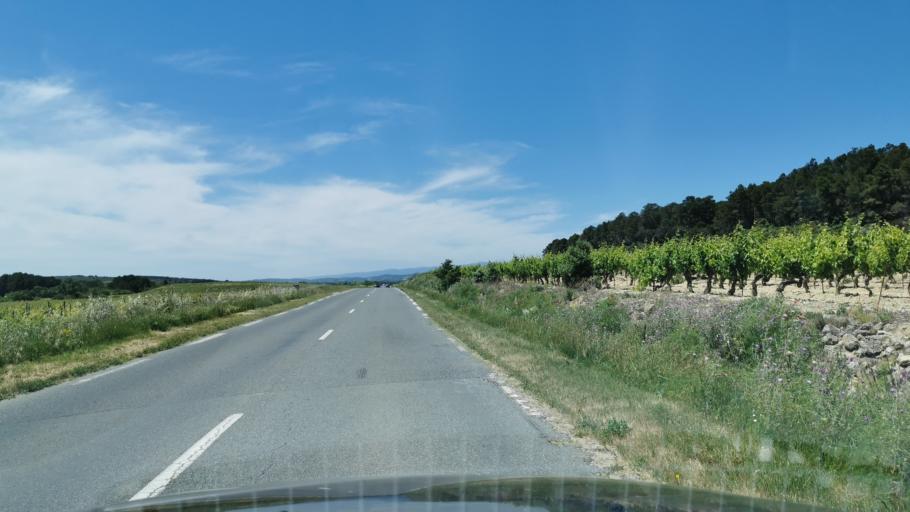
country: FR
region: Languedoc-Roussillon
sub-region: Departement de l'Aude
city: Moussan
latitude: 43.2078
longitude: 2.9529
